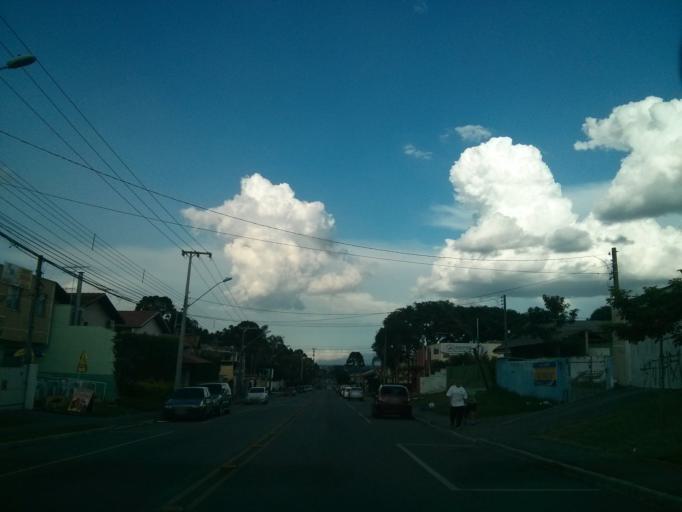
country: BR
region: Parana
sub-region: Sao Jose Dos Pinhais
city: Sao Jose dos Pinhais
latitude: -25.5132
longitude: -49.2400
